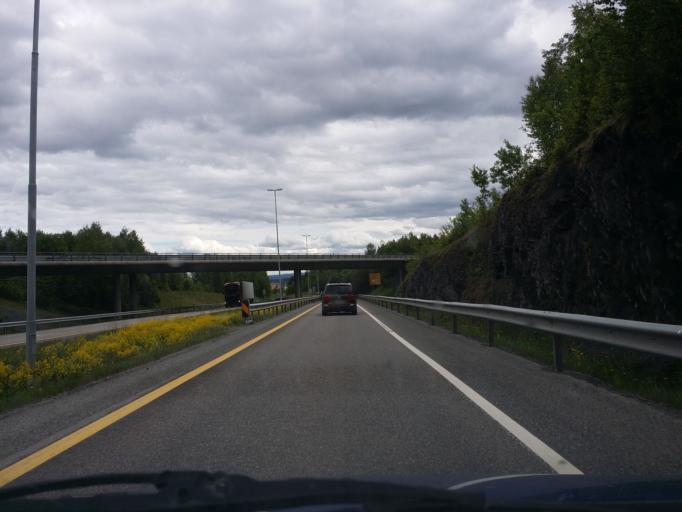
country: NO
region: Hedmark
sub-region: Hamar
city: Hamar
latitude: 60.8448
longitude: 11.0354
